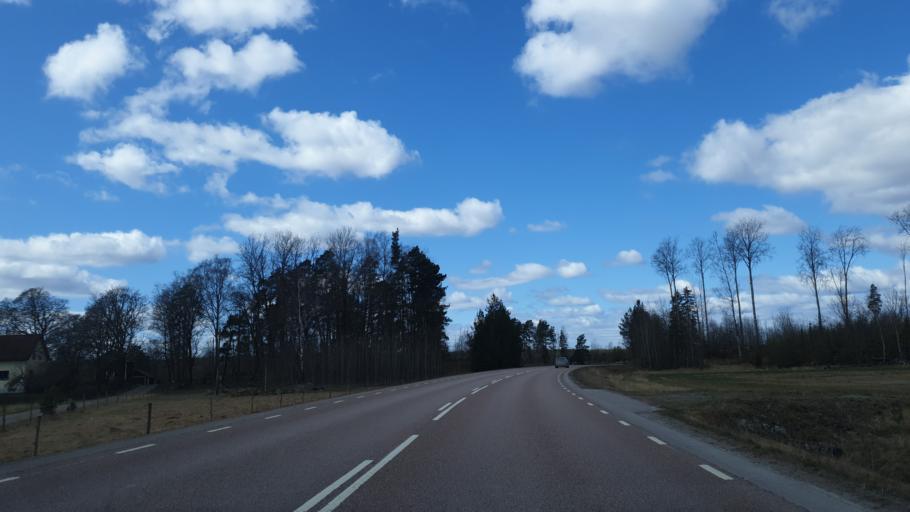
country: SE
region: Vaestmanland
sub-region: Kopings Kommun
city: Koping
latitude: 59.4978
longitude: 15.9404
